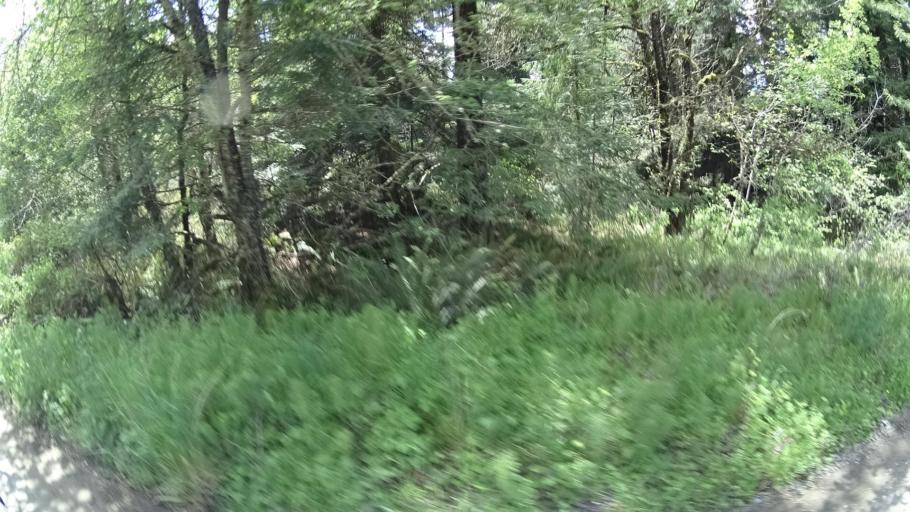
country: US
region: California
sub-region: Humboldt County
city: Blue Lake
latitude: 40.8219
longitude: -123.8923
